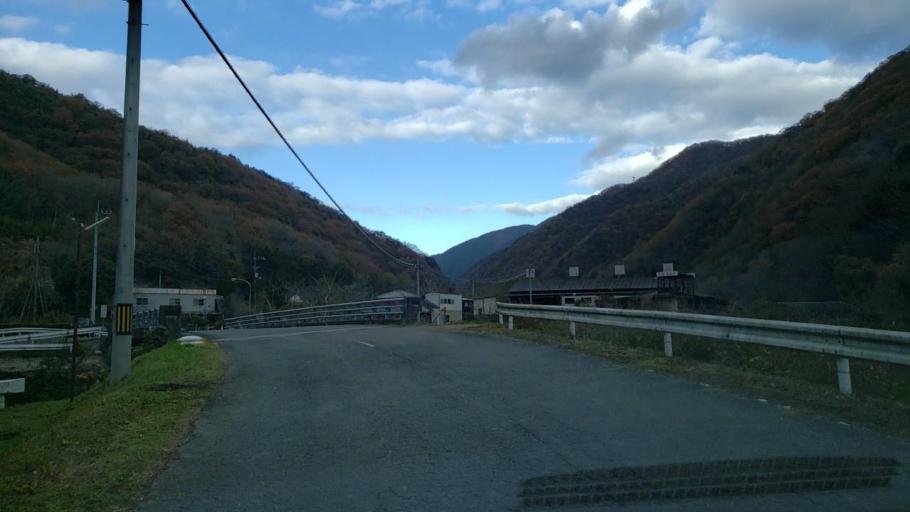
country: JP
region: Tokushima
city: Wakimachi
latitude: 34.1110
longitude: 134.2241
